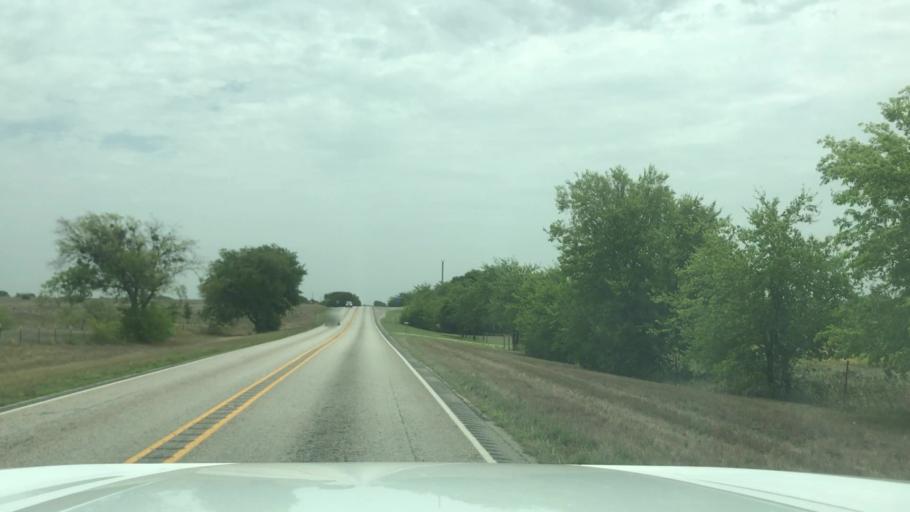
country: US
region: Texas
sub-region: Hamilton County
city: Hico
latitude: 32.0475
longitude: -98.1511
